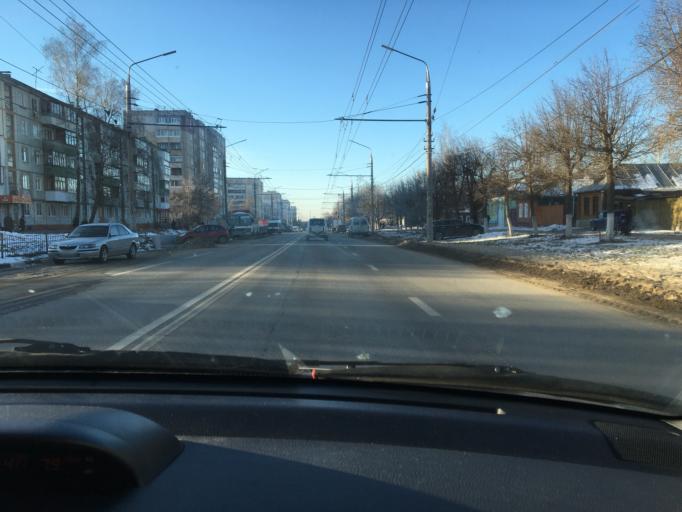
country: RU
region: Tula
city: Tula
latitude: 54.2196
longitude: 37.6132
